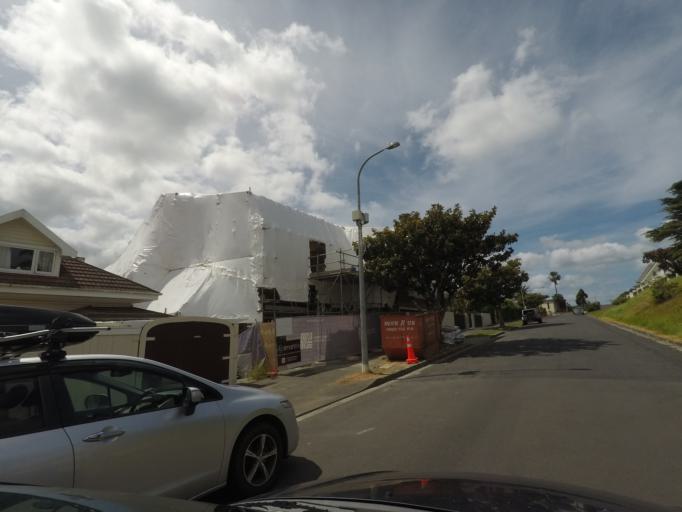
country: NZ
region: Auckland
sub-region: Auckland
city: Auckland
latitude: -36.8456
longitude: 174.7256
